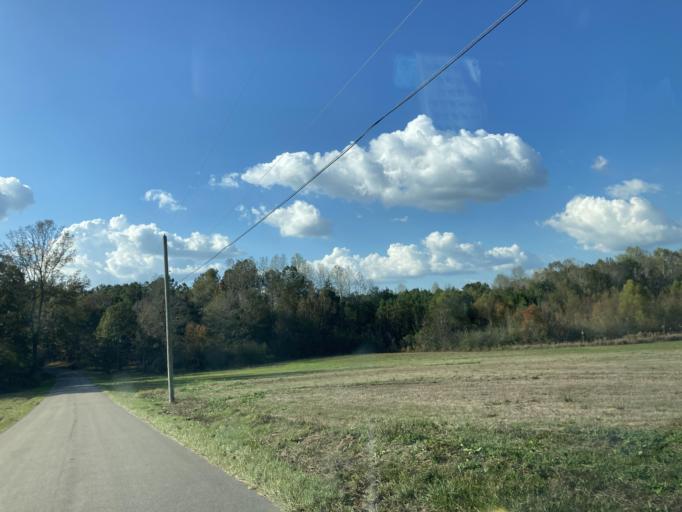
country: US
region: Mississippi
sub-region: Lamar County
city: Sumrall
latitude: 31.4282
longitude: -89.6477
